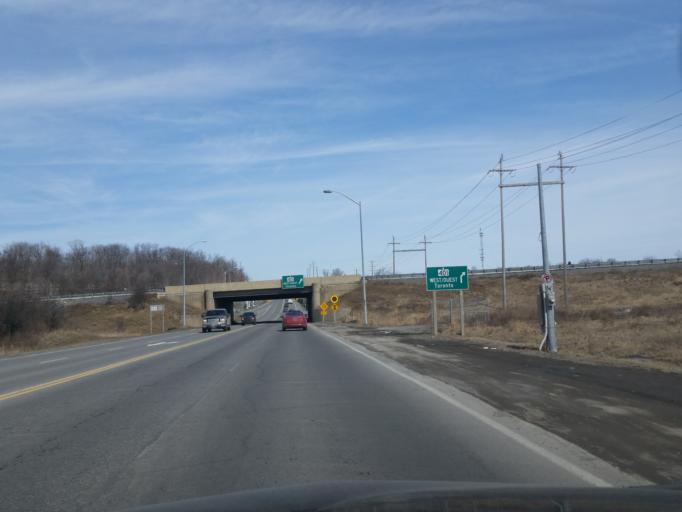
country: CA
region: Ontario
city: Kingston
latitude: 44.2679
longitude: -76.4988
